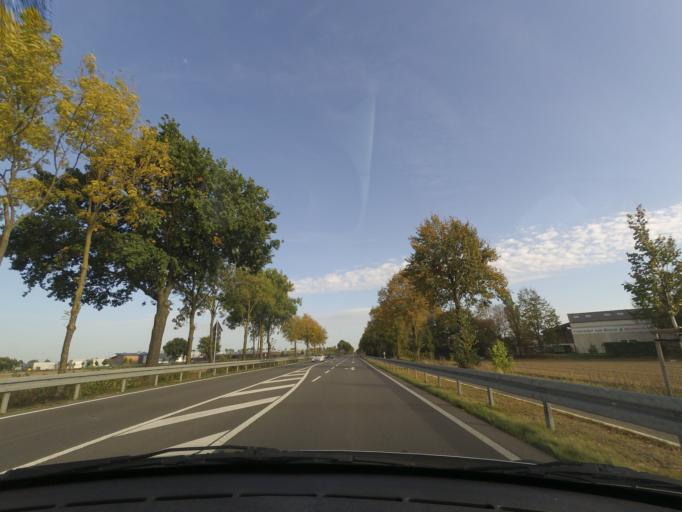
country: DE
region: North Rhine-Westphalia
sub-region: Regierungsbezirk Dusseldorf
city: Kaarst
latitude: 51.1732
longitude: 6.5828
